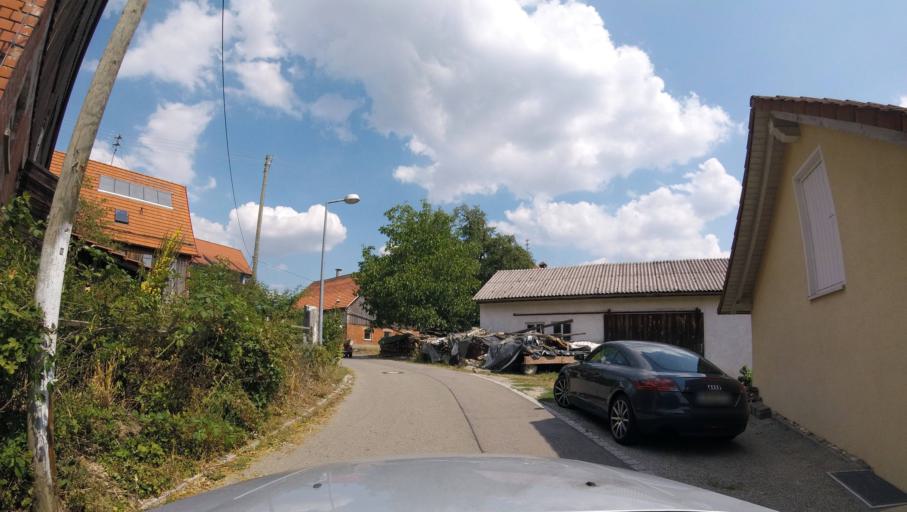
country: DE
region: Baden-Wuerttemberg
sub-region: Regierungsbezirk Stuttgart
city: Alfdorf
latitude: 48.8676
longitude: 9.7296
